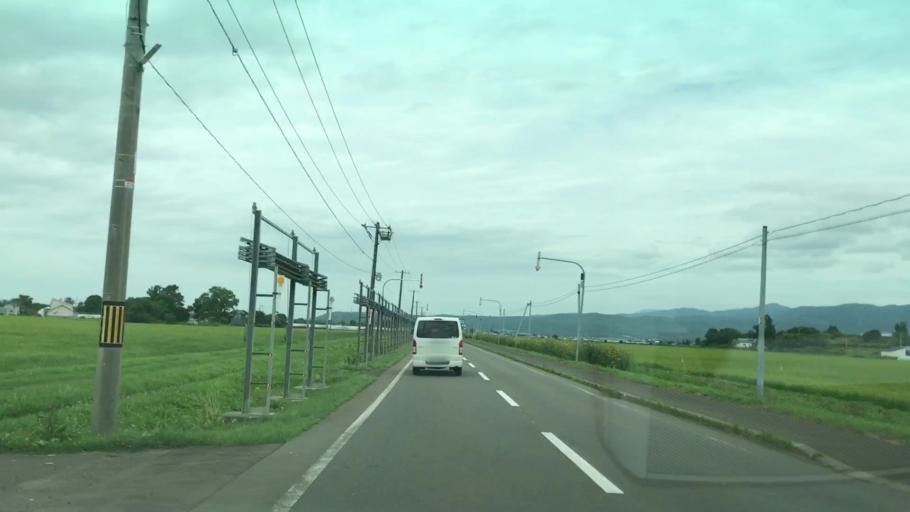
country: JP
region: Hokkaido
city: Iwanai
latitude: 42.9965
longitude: 140.5957
